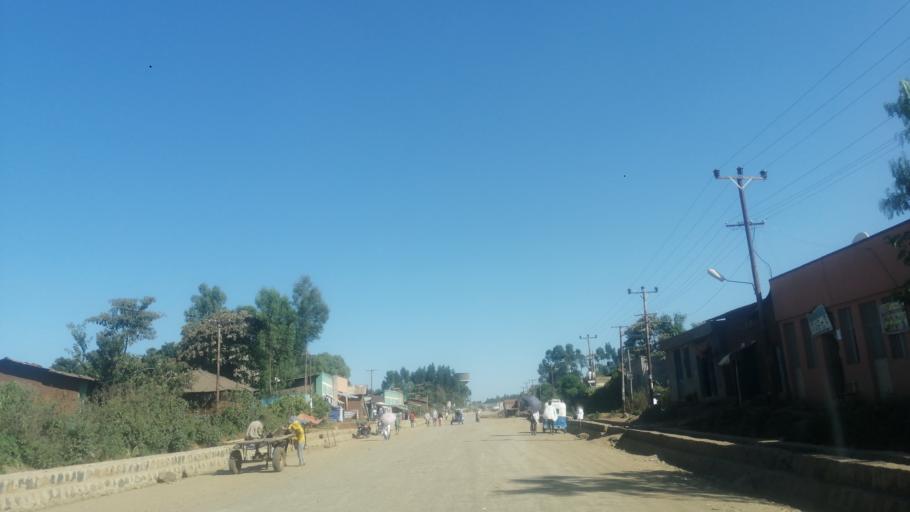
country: ET
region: Amhara
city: Addiet Canna
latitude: 11.0817
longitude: 37.8743
